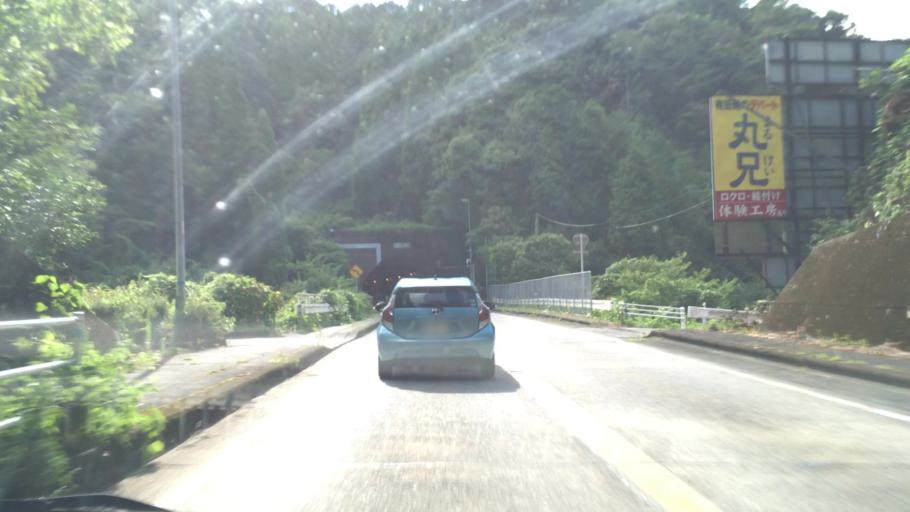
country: JP
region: Saga Prefecture
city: Imaricho-ko
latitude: 33.1884
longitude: 129.9034
